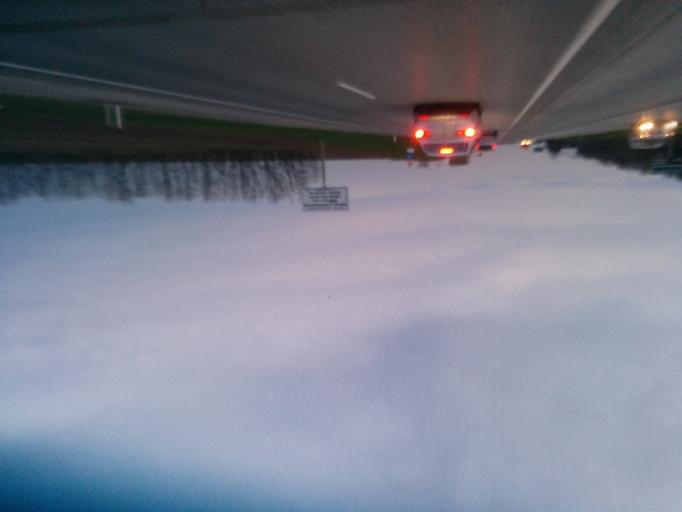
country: RU
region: Rostov
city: Grushevskaya
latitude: 47.5079
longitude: 39.9706
